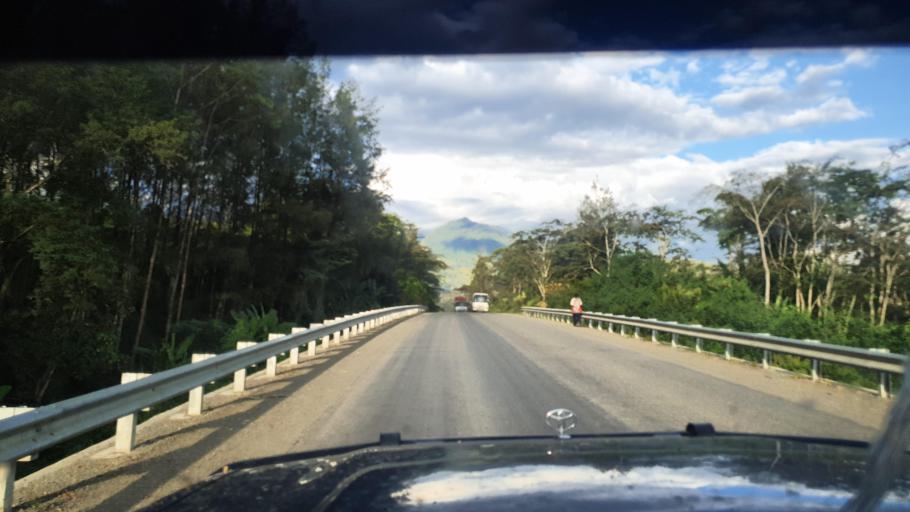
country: PG
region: Chimbu
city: Kundiawa
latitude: -5.9428
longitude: 144.8462
